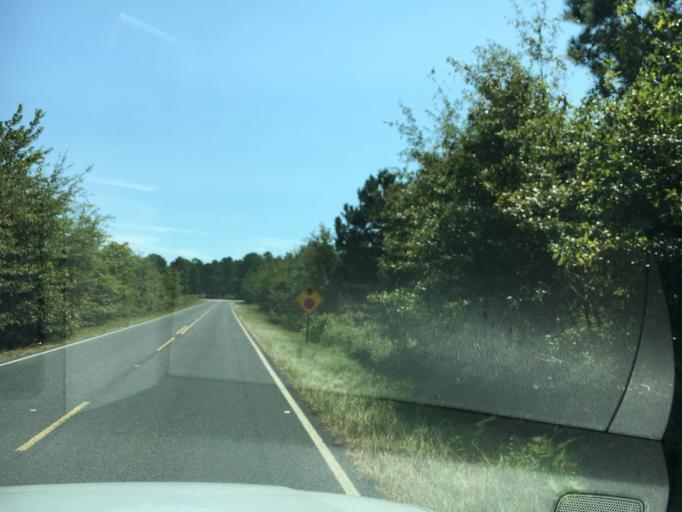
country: US
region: South Carolina
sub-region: Lexington County
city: Batesburg
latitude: 33.8004
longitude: -81.6425
